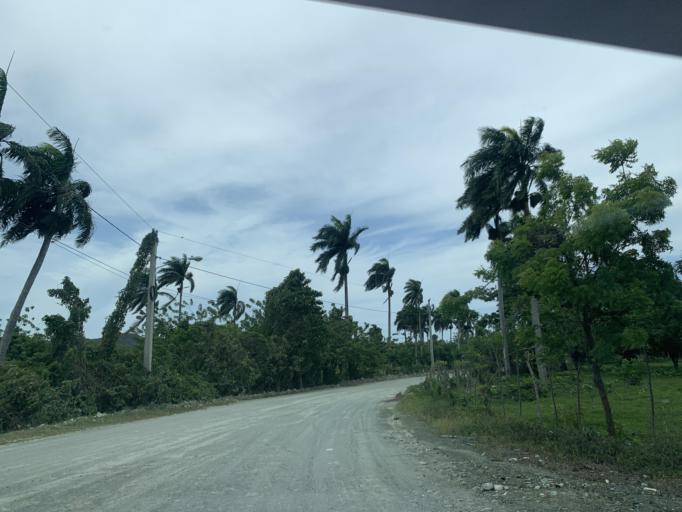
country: DO
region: Puerto Plata
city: Imbert
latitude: 19.8260
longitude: -70.7862
